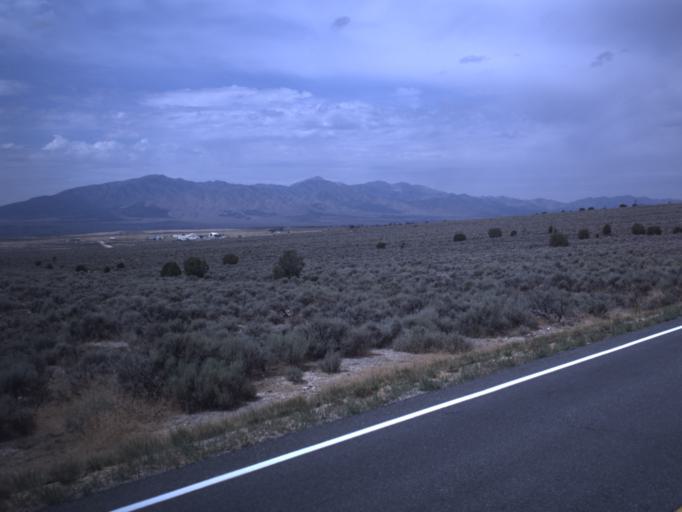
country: US
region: Utah
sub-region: Tooele County
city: Tooele
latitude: 40.3062
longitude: -112.2792
